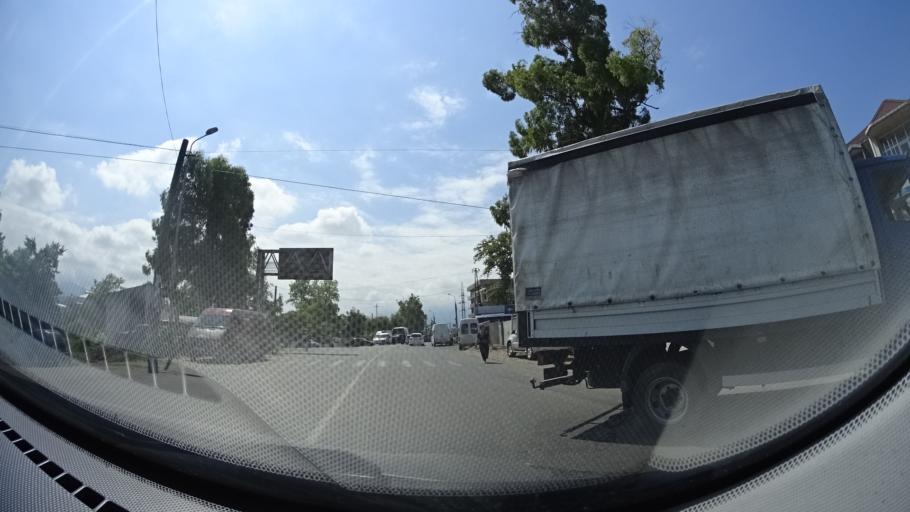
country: GE
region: Ajaria
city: Batumi
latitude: 41.6210
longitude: 41.6164
